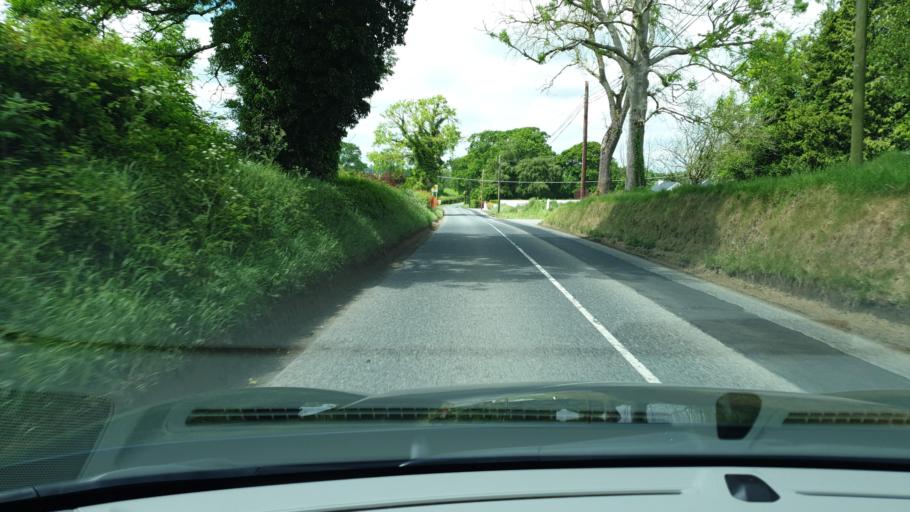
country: IE
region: Ulster
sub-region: An Cabhan
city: Kingscourt
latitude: 53.9002
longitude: -6.7753
